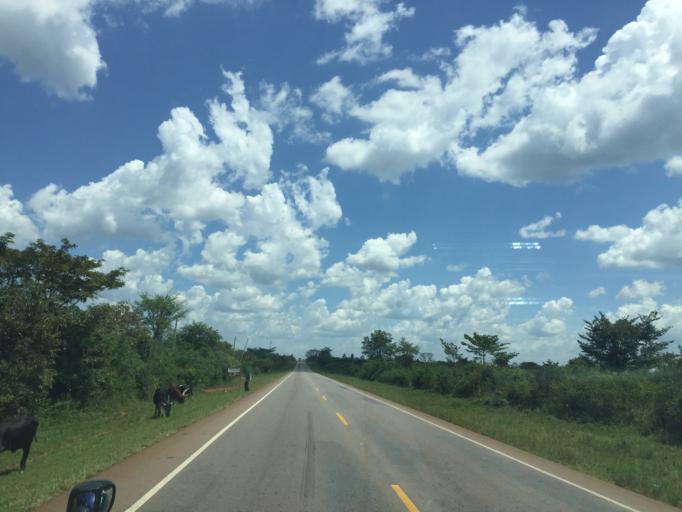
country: UG
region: Central Region
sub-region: Nakasongola District
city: Nakasongola
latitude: 1.3662
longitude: 32.3599
